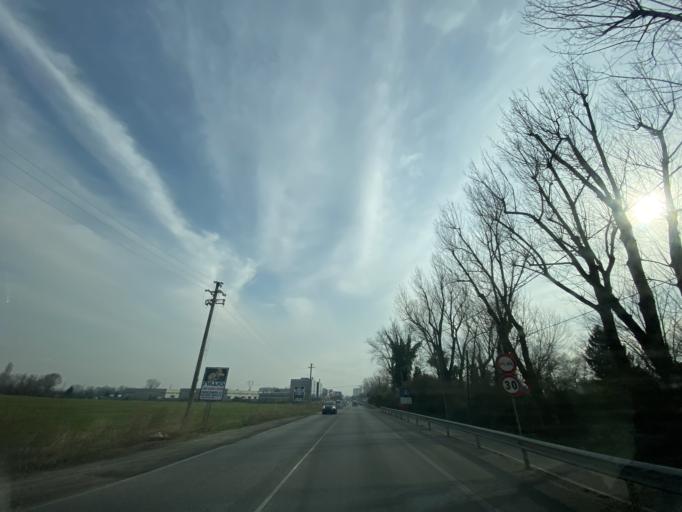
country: IT
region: Lombardy
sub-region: Citta metropolitana di Milano
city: Carugate
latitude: 45.5436
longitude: 9.3352
